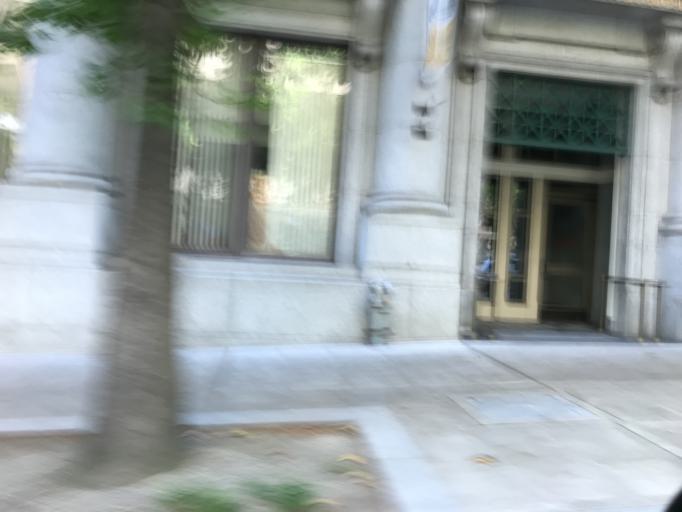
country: US
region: Washington
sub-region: King County
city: Seattle
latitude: 47.6027
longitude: -122.3298
